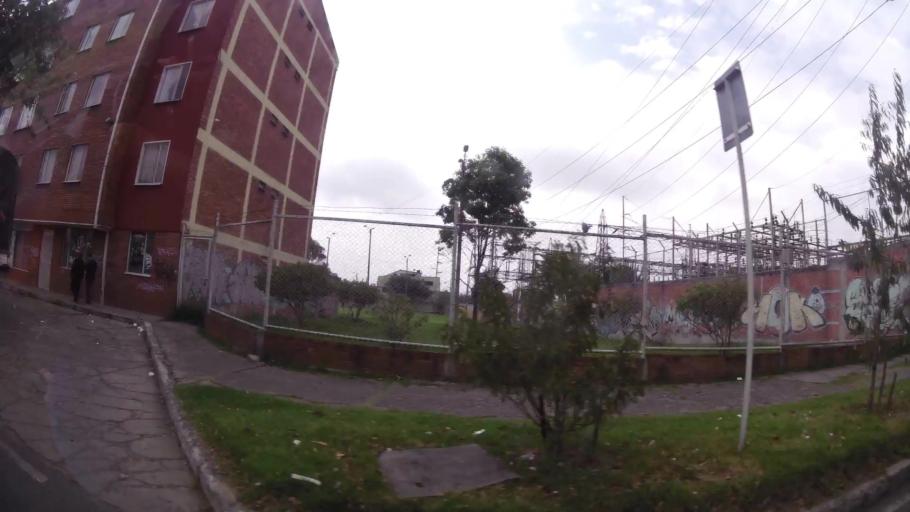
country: CO
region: Bogota D.C.
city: Bogota
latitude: 4.6073
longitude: -74.1077
